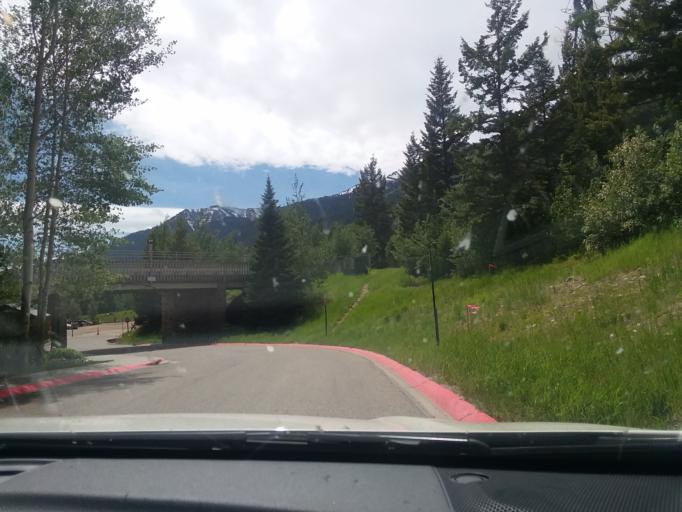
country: US
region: Wyoming
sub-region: Teton County
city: Moose Wilson Road
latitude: 43.5884
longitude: -110.8296
